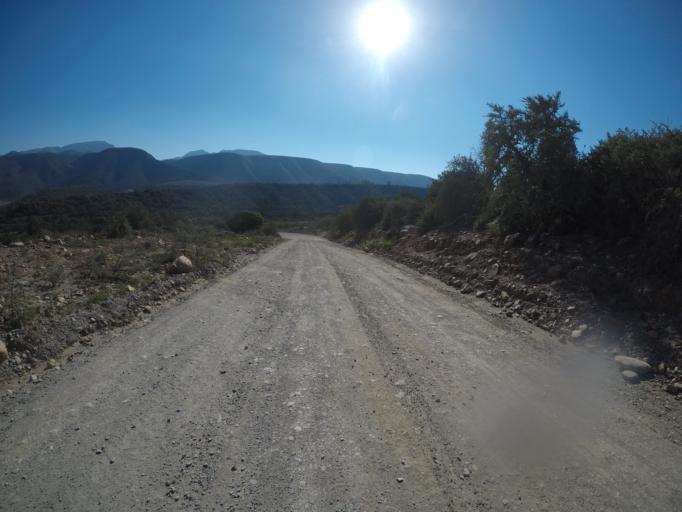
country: ZA
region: Eastern Cape
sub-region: Cacadu District Municipality
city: Kruisfontein
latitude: -33.6700
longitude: 24.5776
